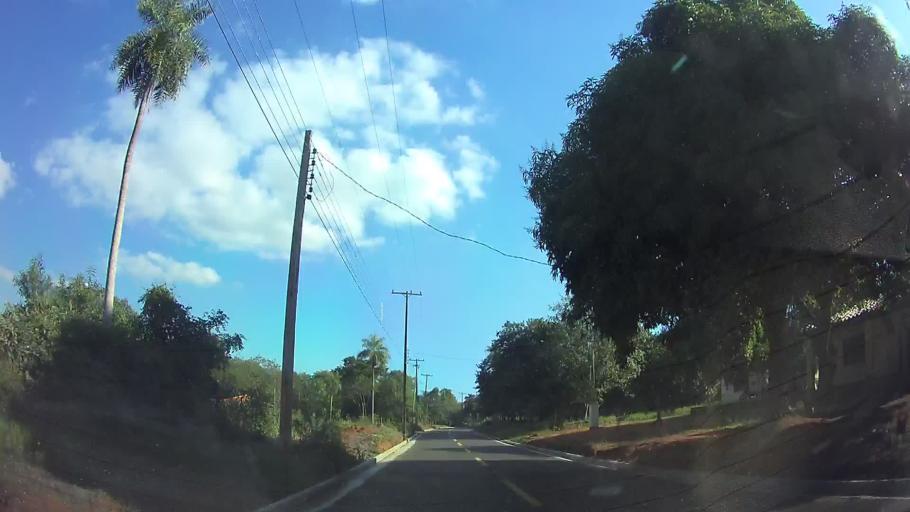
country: PY
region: Central
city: Aregua
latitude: -25.2736
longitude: -57.4397
